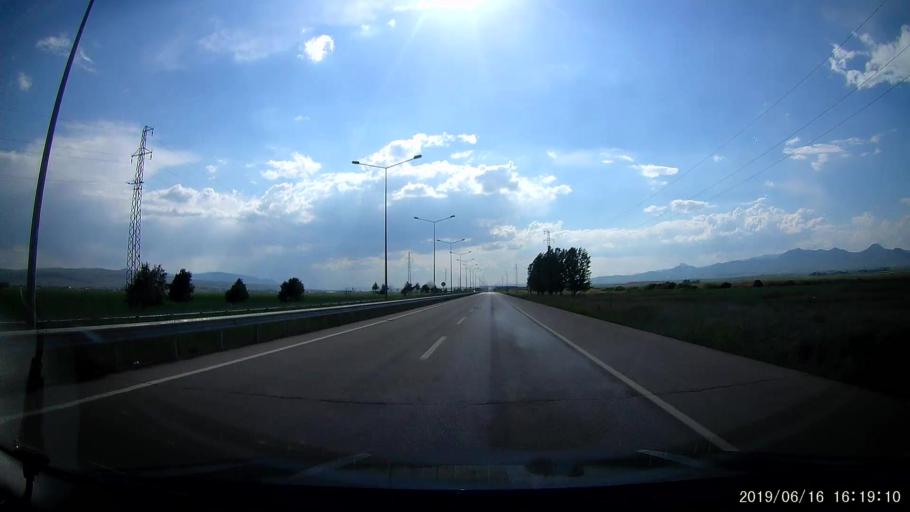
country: TR
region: Erzurum
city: Ilica
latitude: 39.9658
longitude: 41.1487
